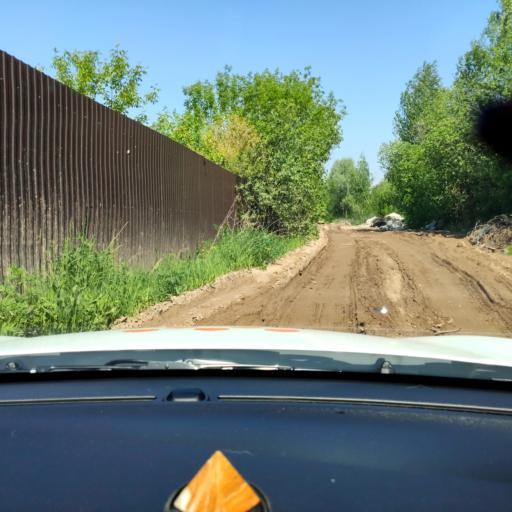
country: RU
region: Tatarstan
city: Stolbishchi
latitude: 55.7053
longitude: 49.1826
